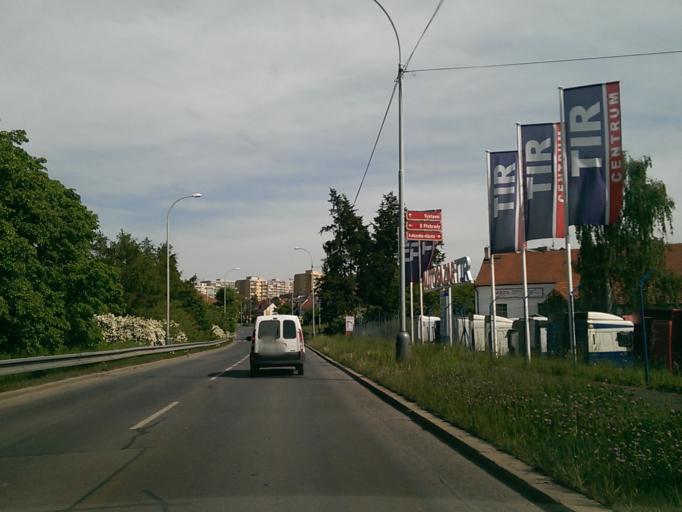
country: CZ
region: Central Bohemia
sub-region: Okres Praha-Zapad
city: Pruhonice
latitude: 50.0371
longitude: 14.5239
